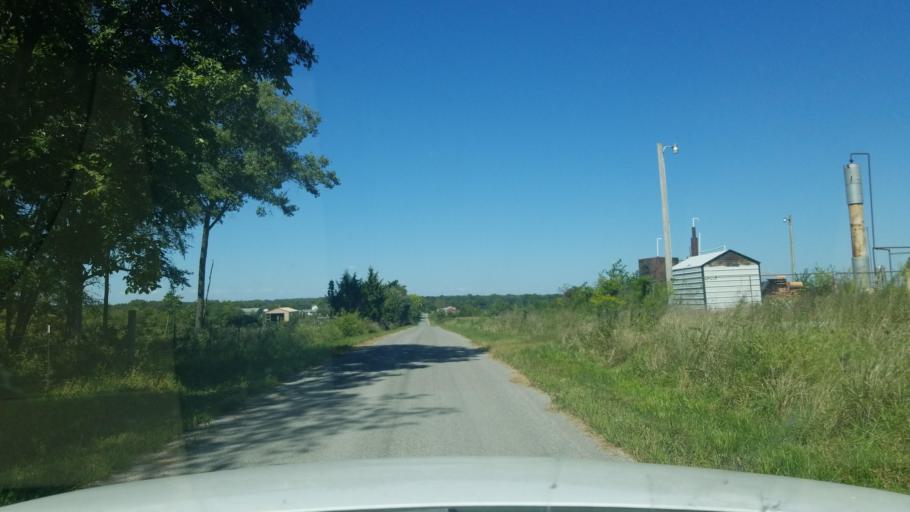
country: US
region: Illinois
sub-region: Saline County
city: Eldorado
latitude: 37.8557
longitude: -88.5119
